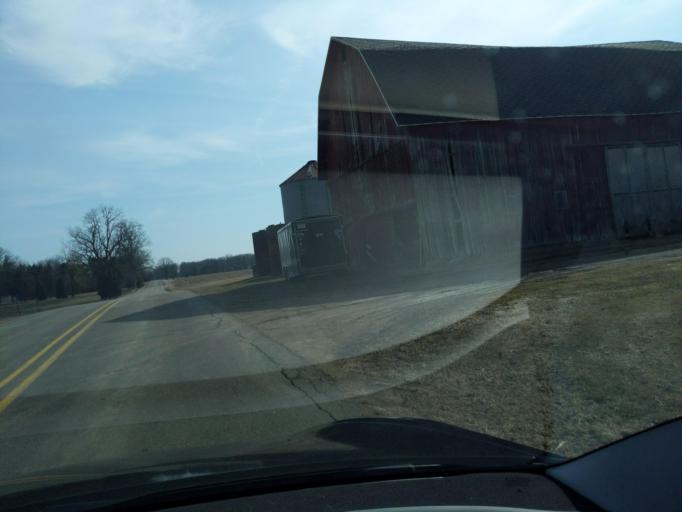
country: US
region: Michigan
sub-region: Ingham County
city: Webberville
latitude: 42.6591
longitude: -84.2159
